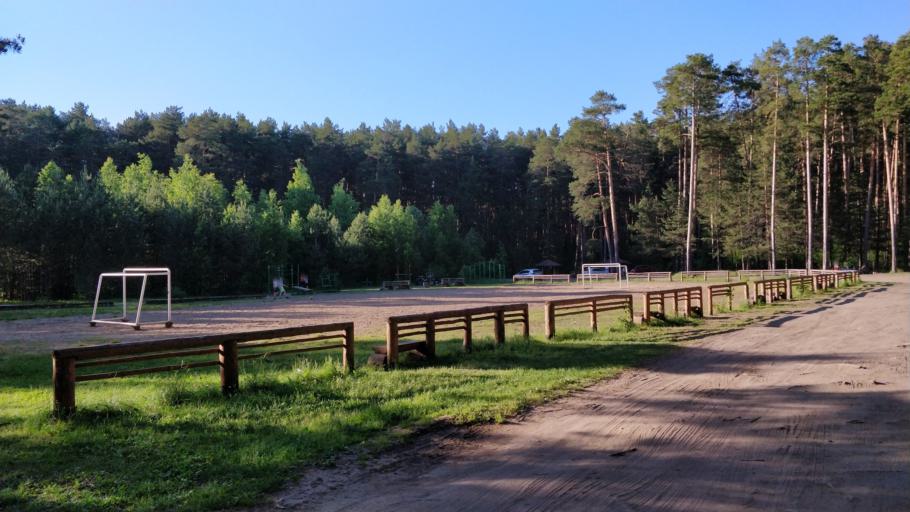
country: RU
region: Perm
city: Perm
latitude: 58.0586
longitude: 56.2850
